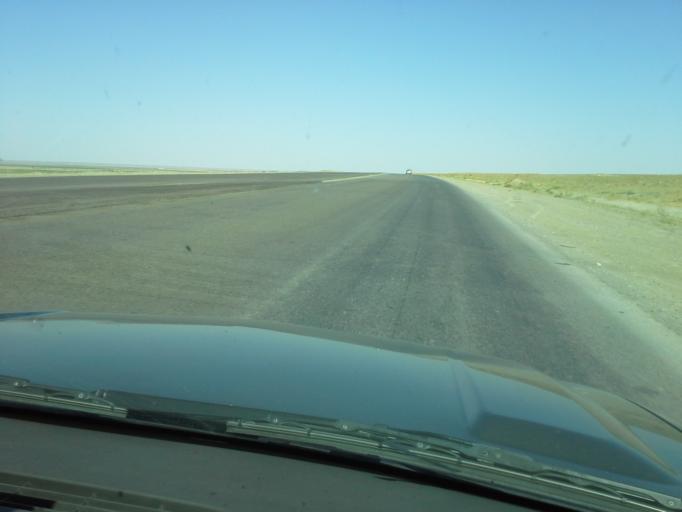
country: TM
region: Ahal
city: Baharly
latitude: 38.6396
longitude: 56.9316
